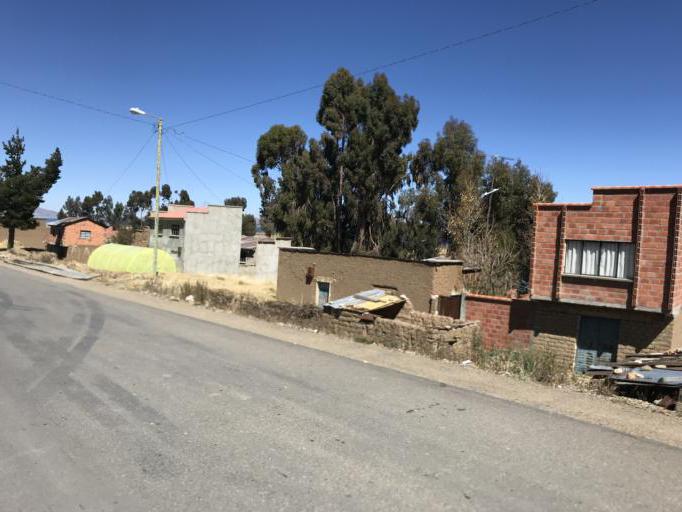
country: BO
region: La Paz
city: Huatajata
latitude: -16.1998
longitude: -68.7134
